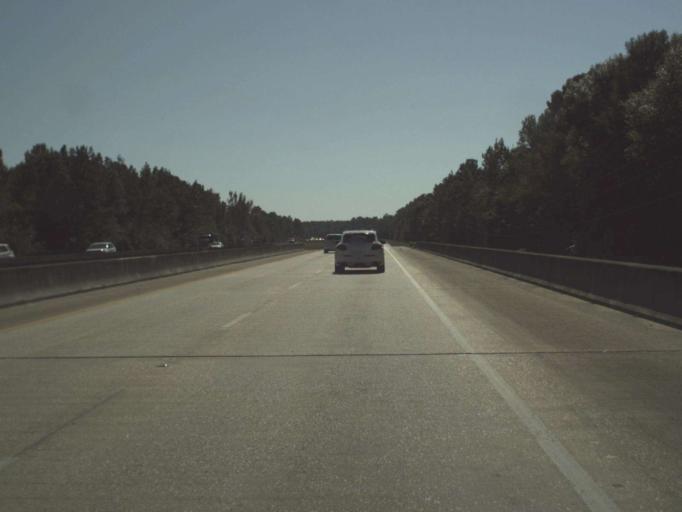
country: US
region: Florida
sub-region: Okaloosa County
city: Crestview
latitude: 30.6963
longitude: -86.5718
